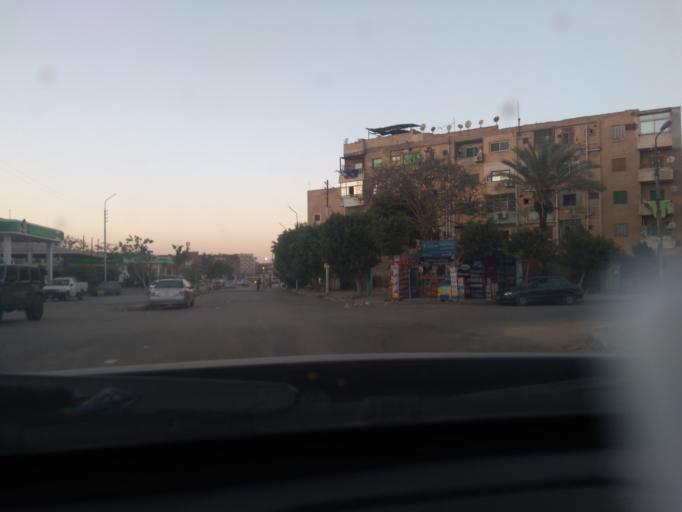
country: EG
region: Muhafazat al Qahirah
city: Cairo
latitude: 30.0823
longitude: 31.3514
